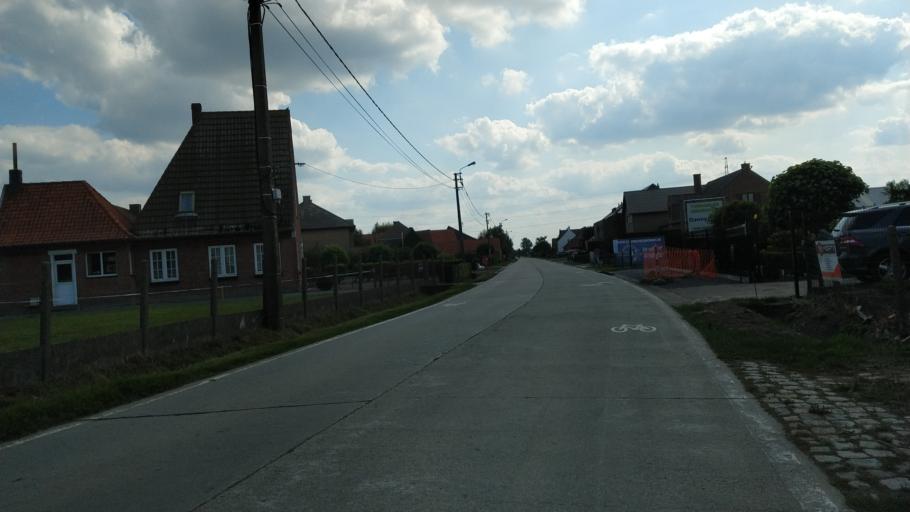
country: BE
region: Flanders
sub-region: Provincie Oost-Vlaanderen
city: Evergem
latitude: 51.1508
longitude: 3.6939
